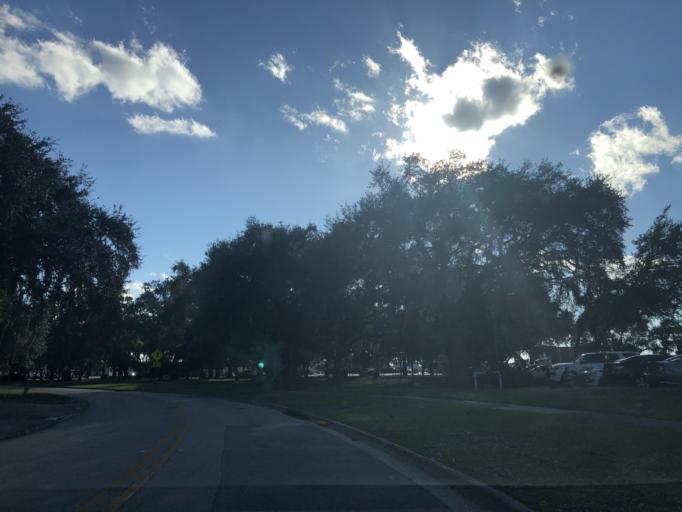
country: US
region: Florida
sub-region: Osceola County
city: Saint Cloud
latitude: 28.2546
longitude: -81.3144
